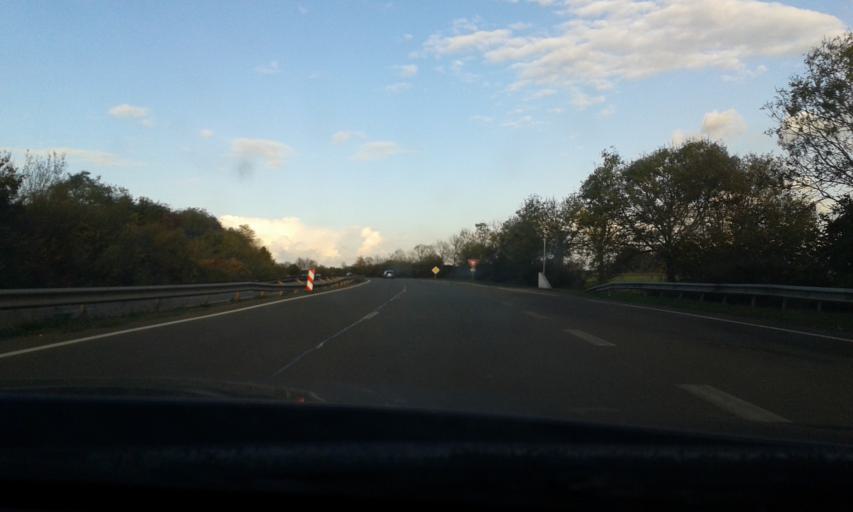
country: FR
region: Centre
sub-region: Departement d'Eure-et-Loir
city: Le Coudray
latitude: 48.4166
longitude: 1.5046
